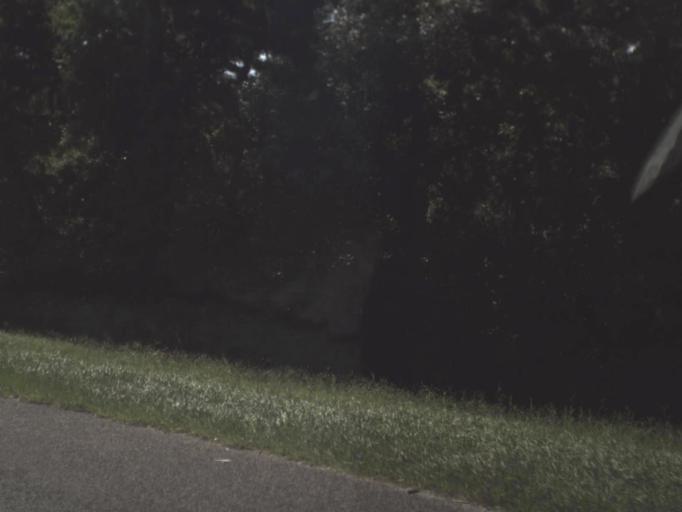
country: US
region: Florida
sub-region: Hernando County
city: Brooksville
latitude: 28.5390
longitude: -82.3745
